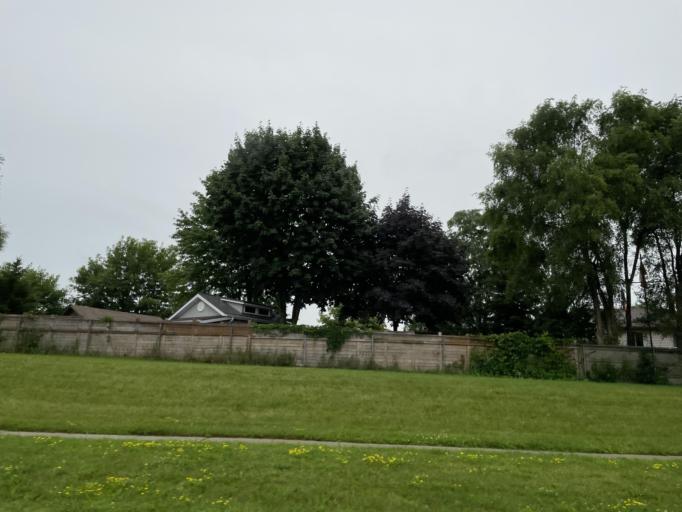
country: CA
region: Ontario
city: Cambridge
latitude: 43.3932
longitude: -80.3069
